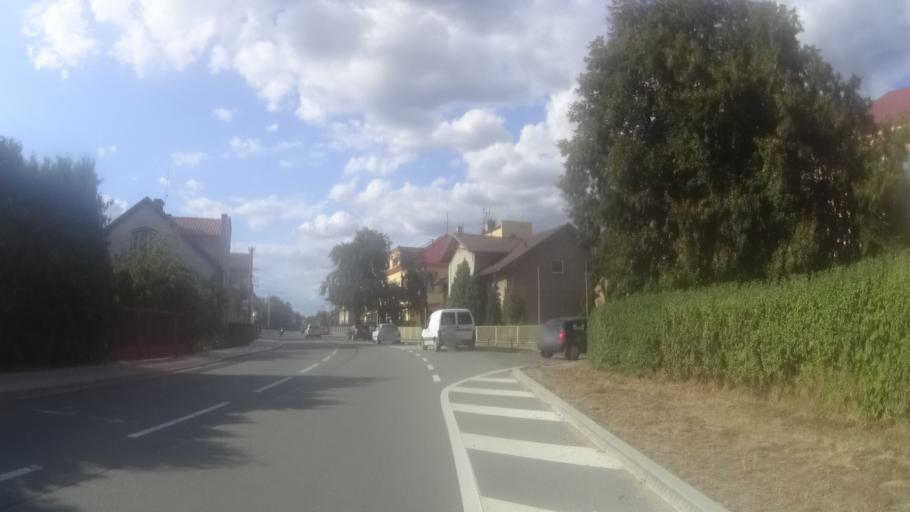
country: CZ
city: Albrechtice nad Orlici
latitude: 50.1405
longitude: 16.0635
